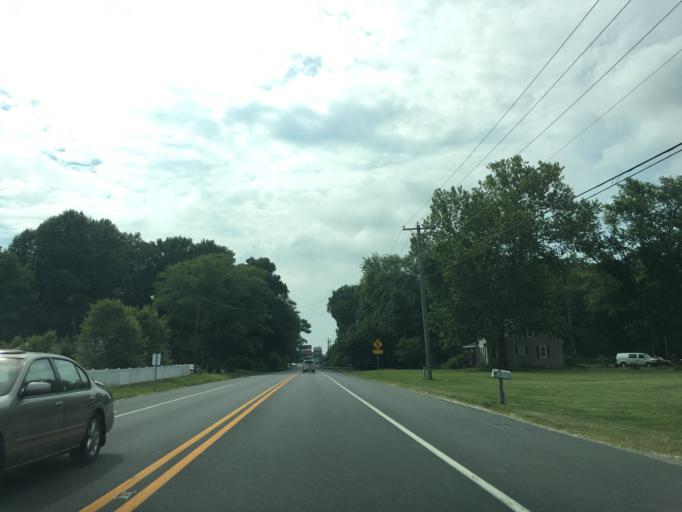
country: US
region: Delaware
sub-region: Sussex County
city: Millsboro
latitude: 38.5633
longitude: -75.2720
